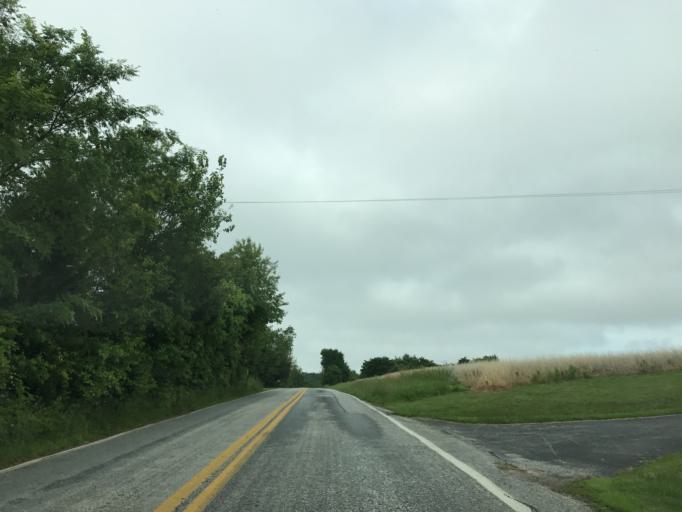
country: US
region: Pennsylvania
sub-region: York County
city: Susquehanna Trails
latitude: 39.7451
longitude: -76.4408
